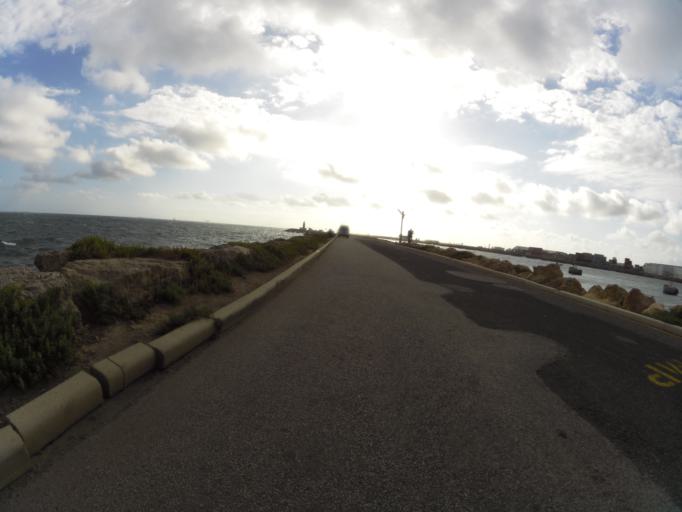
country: AU
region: Western Australia
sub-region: Fremantle
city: South Fremantle
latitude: -32.0563
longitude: 115.7371
